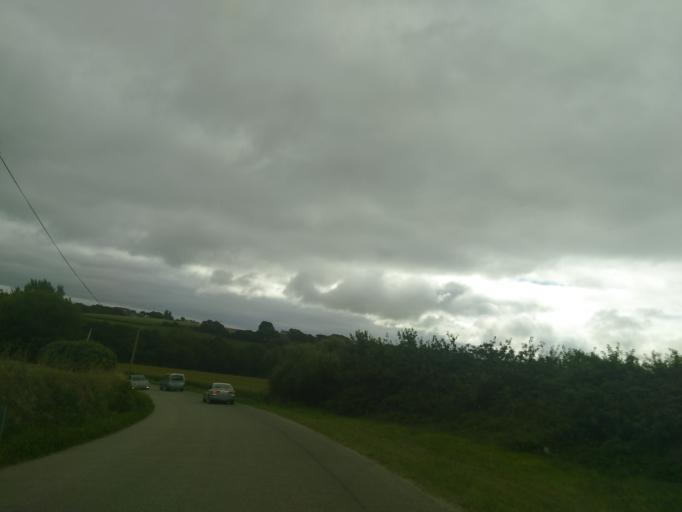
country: FR
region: Brittany
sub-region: Departement du Finistere
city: Plomodiern
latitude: 48.1605
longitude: -4.2560
